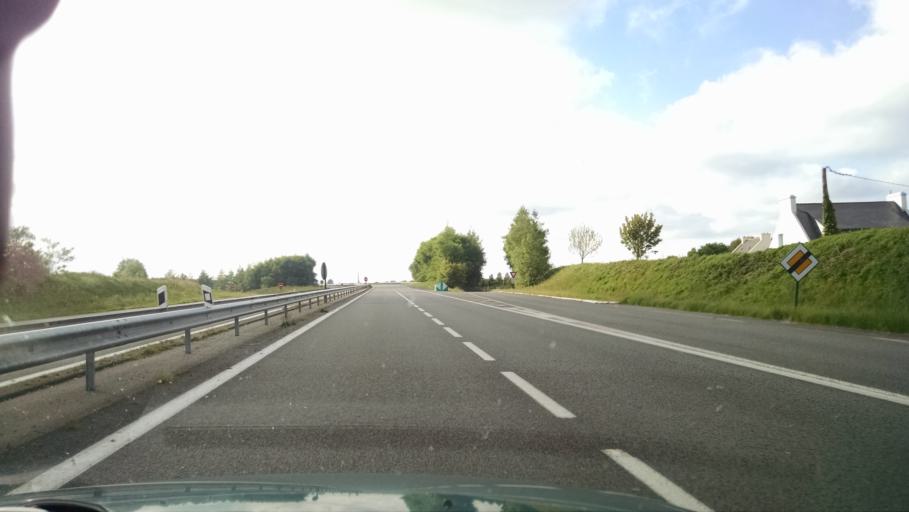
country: FR
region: Brittany
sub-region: Departement du Finistere
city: Taule
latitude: 48.6184
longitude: -3.8966
